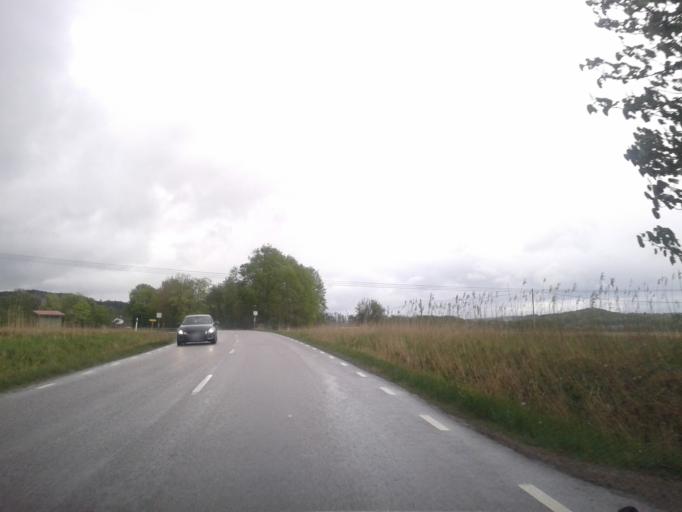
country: SE
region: Vaestra Goetaland
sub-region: Ale Kommun
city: Alafors
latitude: 57.9478
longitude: 12.0679
